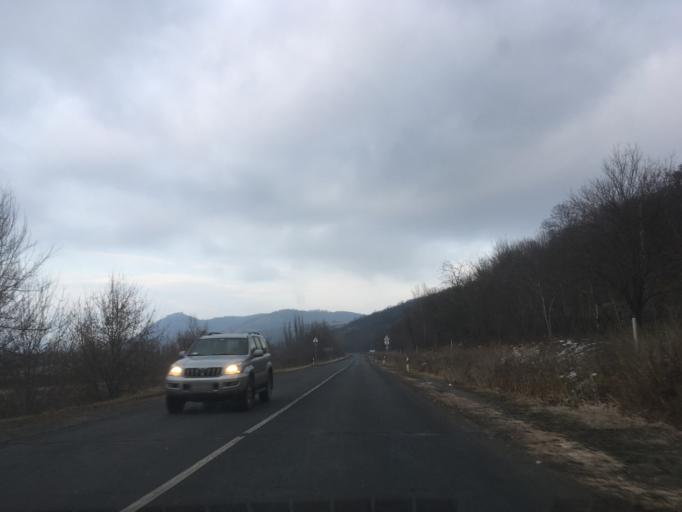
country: HU
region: Pest
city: Visegrad
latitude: 47.7666
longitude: 18.9548
